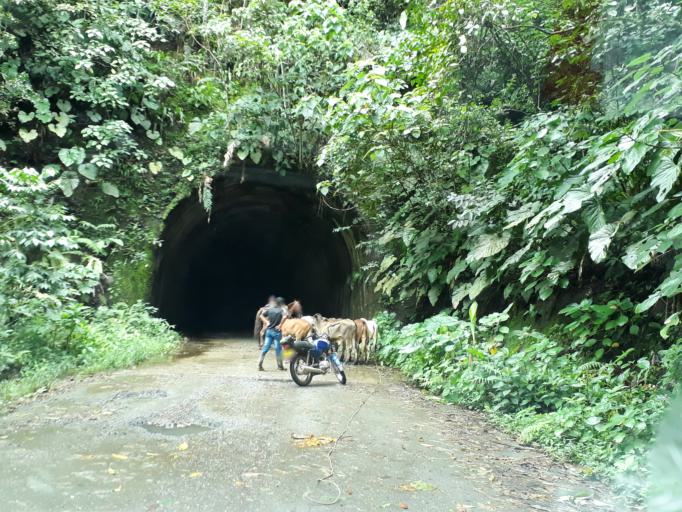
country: CO
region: Boyaca
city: Santa Maria
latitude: 4.7307
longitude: -73.3064
